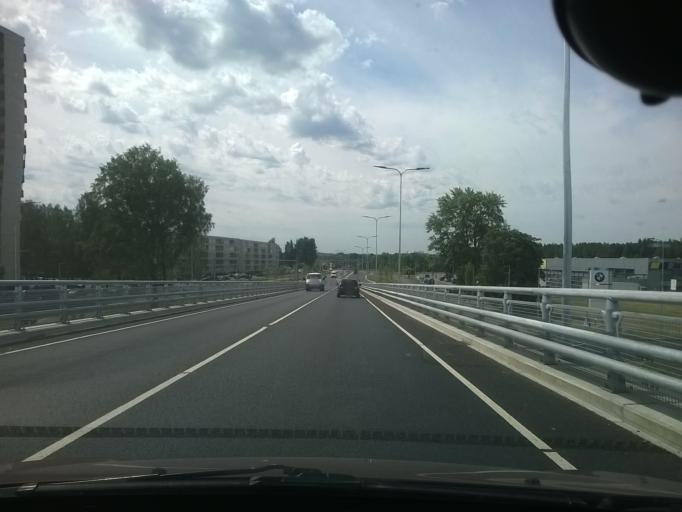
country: EE
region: Harju
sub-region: Saue vald
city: Laagri
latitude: 59.4225
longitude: 24.6447
